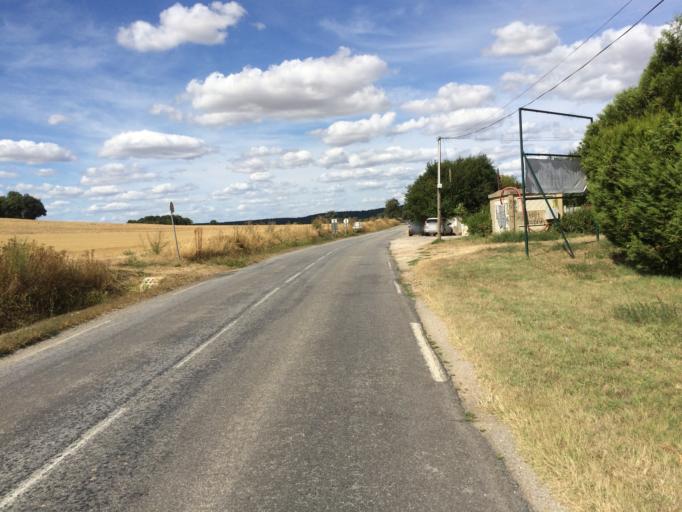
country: FR
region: Ile-de-France
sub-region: Departement de l'Essonne
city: Maisse
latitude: 48.4070
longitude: 2.3794
